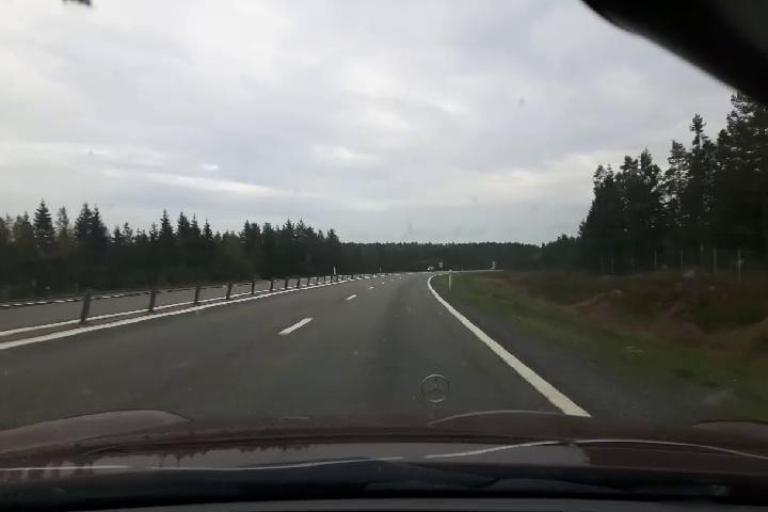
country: SE
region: Vaesternorrland
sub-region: Haernoesands Kommun
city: Haernoesand
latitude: 62.7245
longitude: 17.9222
